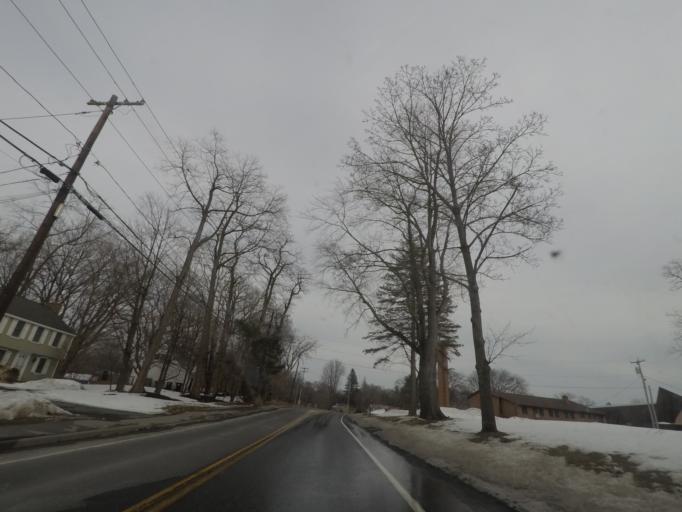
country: US
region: New York
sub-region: Albany County
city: Delmar
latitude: 42.6114
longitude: -73.8477
